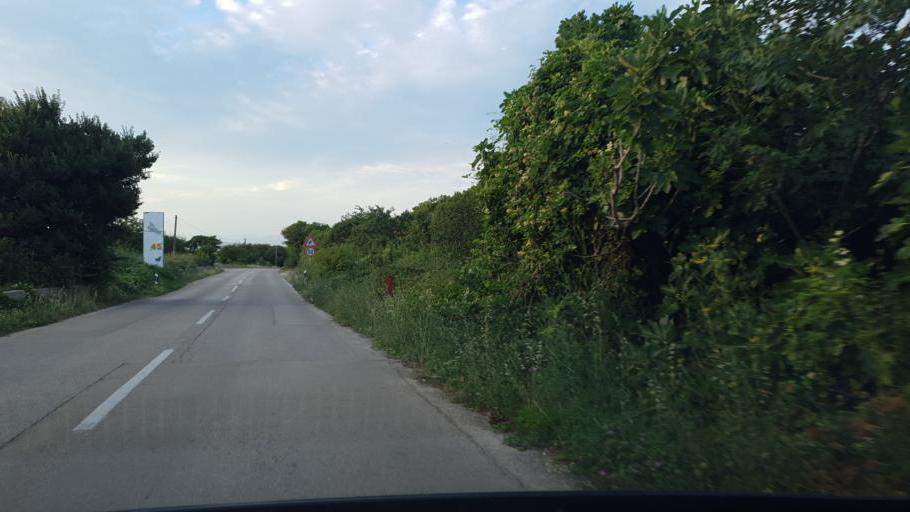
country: HR
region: Primorsko-Goranska
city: Punat
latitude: 45.0018
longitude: 14.6335
